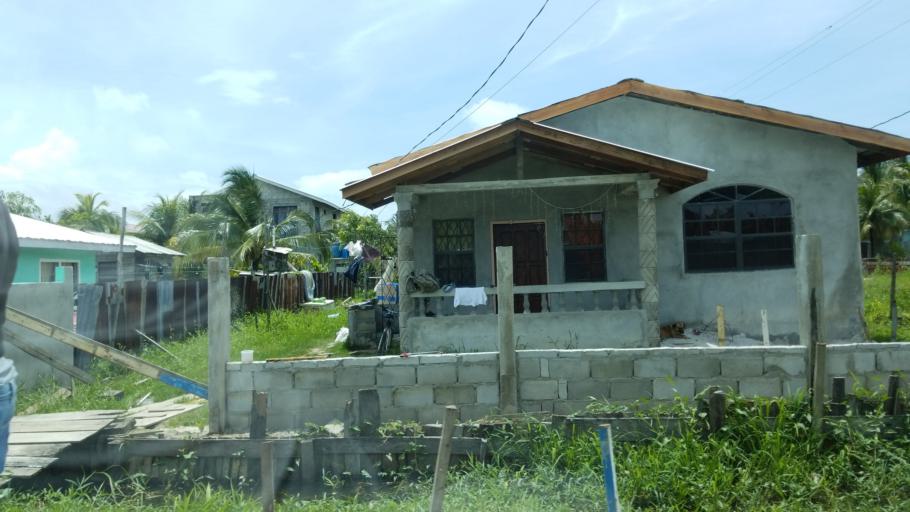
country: GY
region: Demerara-Mahaica
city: Georgetown
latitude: 6.7921
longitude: -58.1234
